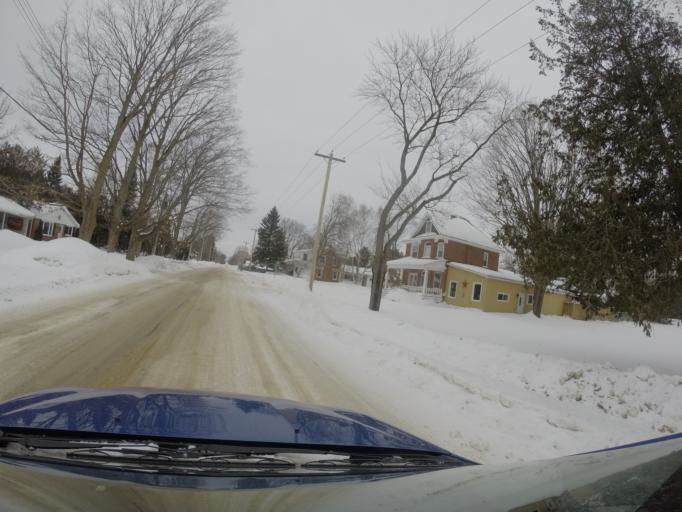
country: CA
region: Ontario
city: Wasaga Beach
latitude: 44.4188
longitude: -80.0797
